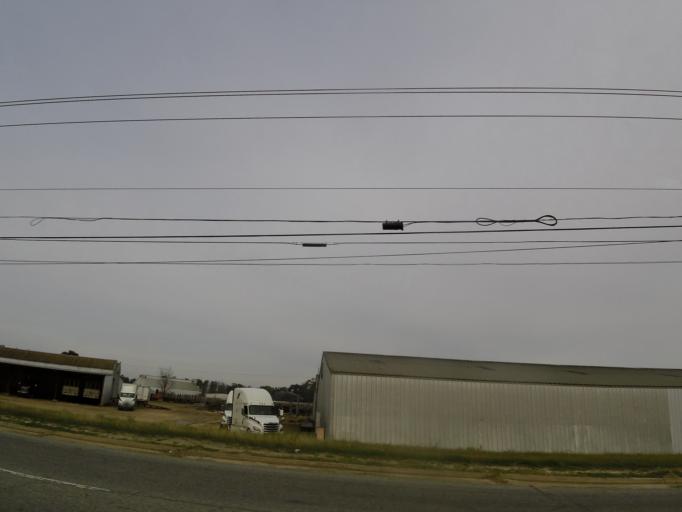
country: US
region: Georgia
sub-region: Decatur County
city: Bainbridge
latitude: 30.9136
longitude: -84.5855
